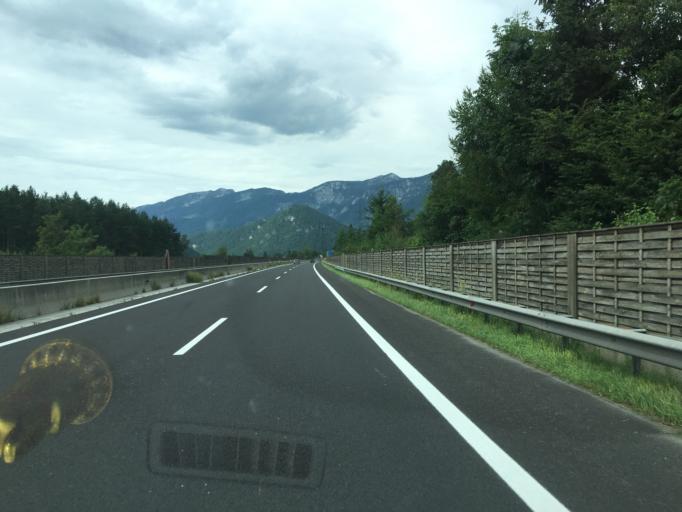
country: AT
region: Upper Austria
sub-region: Politischer Bezirk Kirchdorf an der Krems
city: Rossleithen
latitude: 47.7104
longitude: 14.3072
